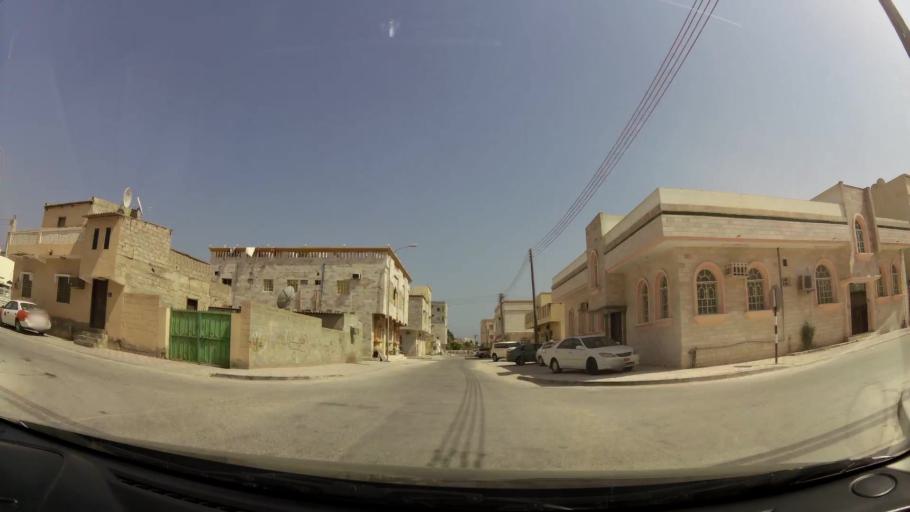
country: OM
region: Zufar
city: Salalah
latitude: 17.0138
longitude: 54.0596
